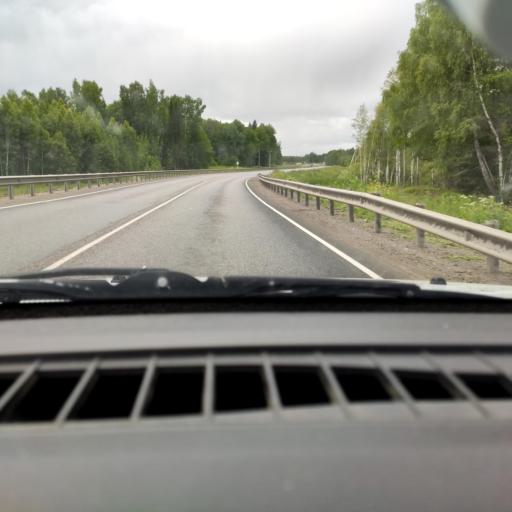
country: RU
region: Perm
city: Kungur
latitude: 57.3331
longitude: 56.9652
